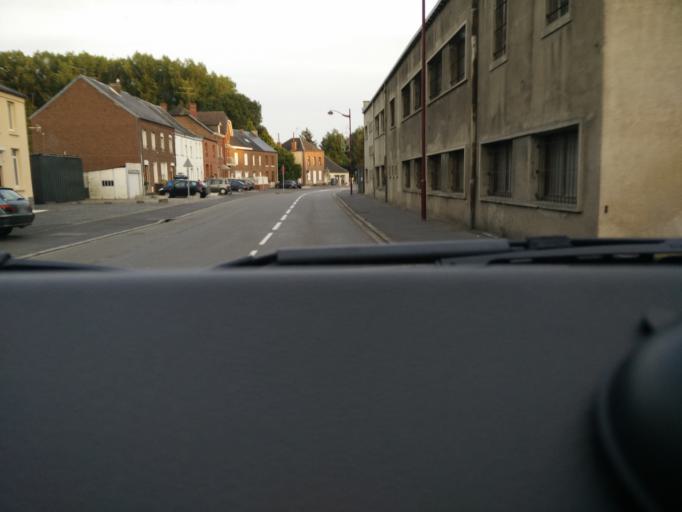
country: FR
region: Nord-Pas-de-Calais
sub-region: Departement du Nord
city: Pont-sur-Sambre
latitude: 50.2189
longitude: 3.8490
